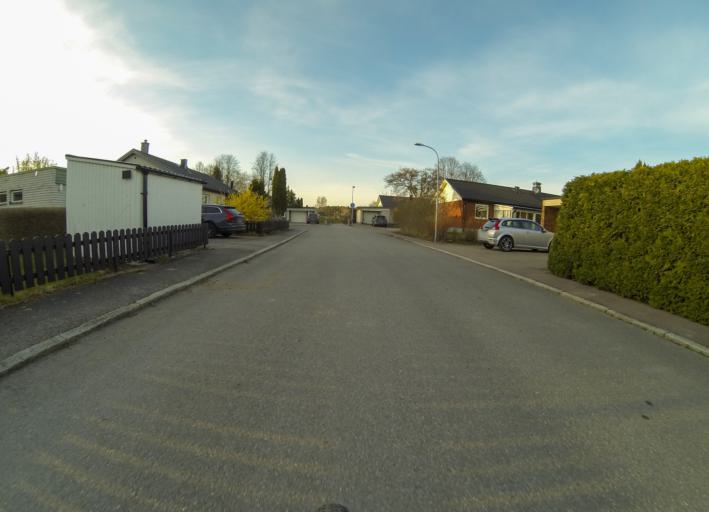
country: SE
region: Vaestmanland
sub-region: Vasteras
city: Vasteras
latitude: 59.5974
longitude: 16.6100
